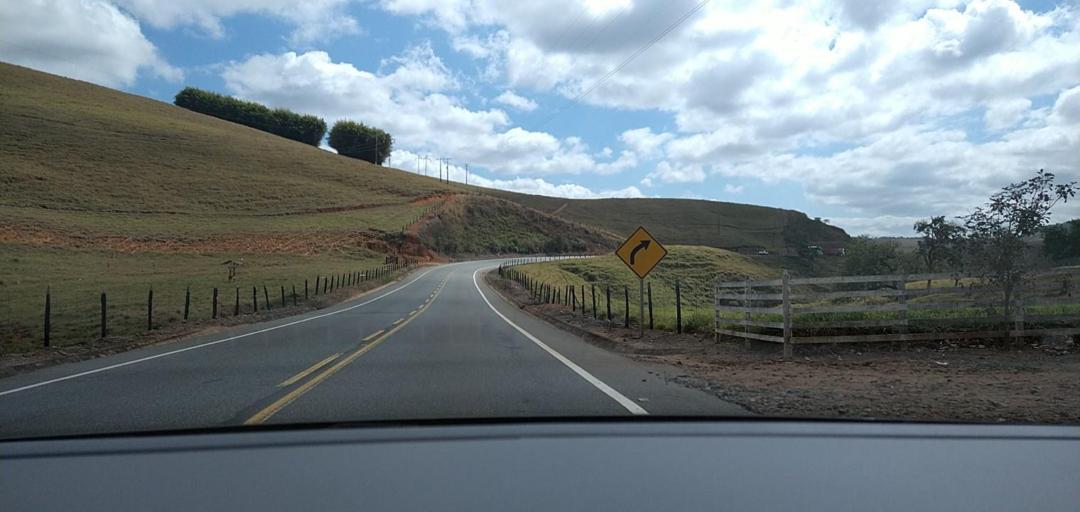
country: BR
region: Minas Gerais
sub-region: Ponte Nova
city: Ponte Nova
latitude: -20.4908
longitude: -42.8800
